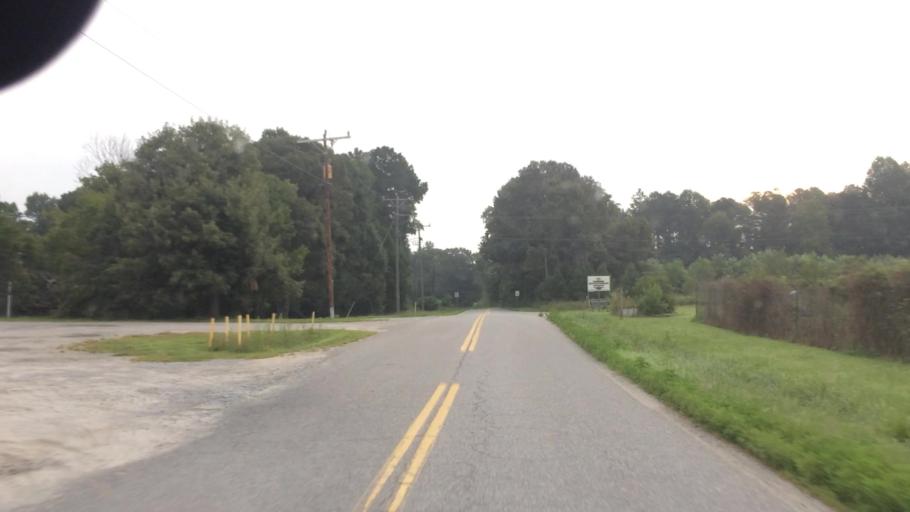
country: US
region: Virginia
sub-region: King William County
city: West Point
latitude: 37.5511
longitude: -76.7157
